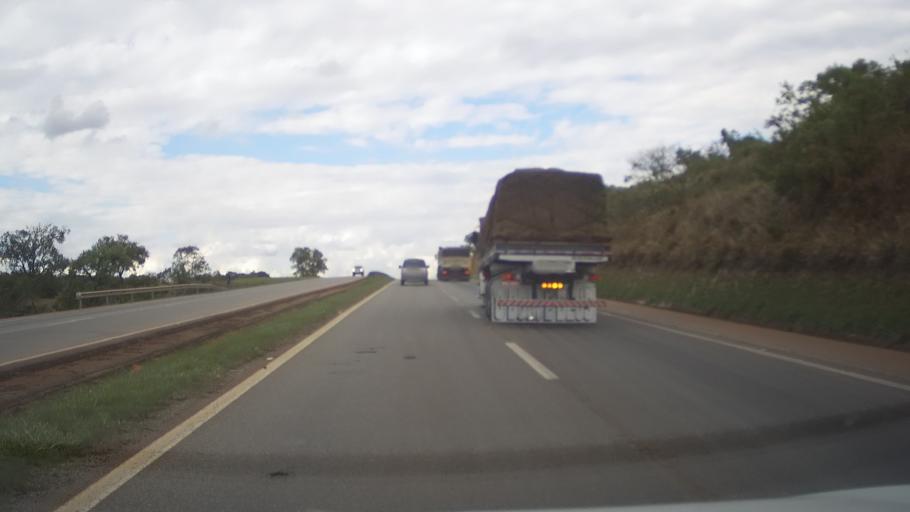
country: BR
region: Minas Gerais
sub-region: Itauna
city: Itauna
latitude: -20.3097
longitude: -44.4495
